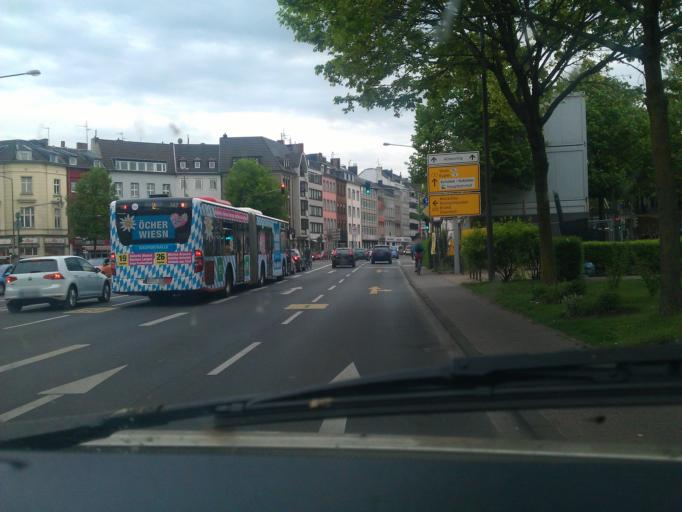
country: DE
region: North Rhine-Westphalia
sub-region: Regierungsbezirk Koln
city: Aachen
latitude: 50.7753
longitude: 6.0958
